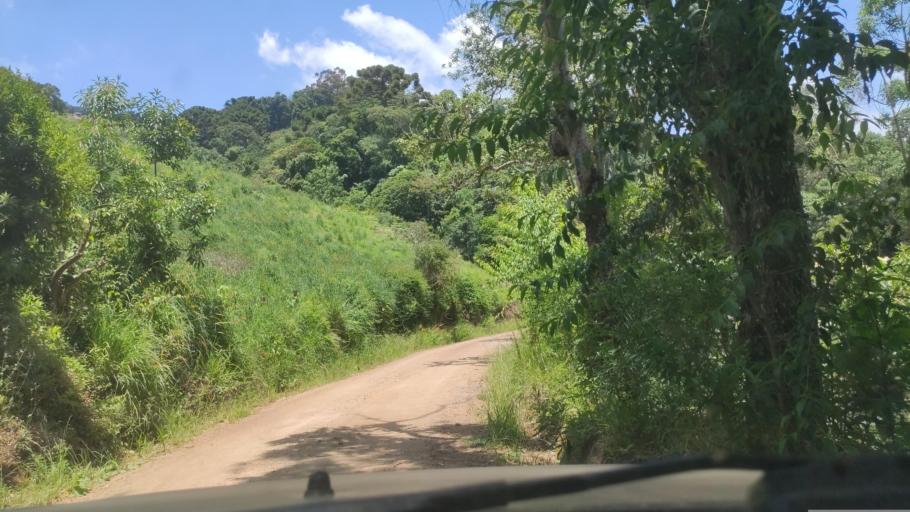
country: BR
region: Minas Gerais
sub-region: Cambui
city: Cambui
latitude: -22.6738
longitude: -45.9647
